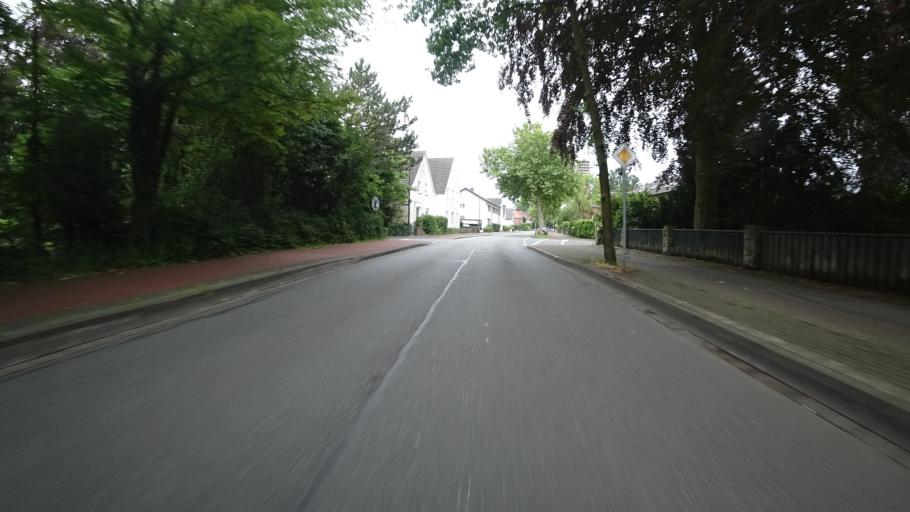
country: DE
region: North Rhine-Westphalia
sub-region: Regierungsbezirk Detmold
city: Guetersloh
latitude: 51.9300
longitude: 8.3843
